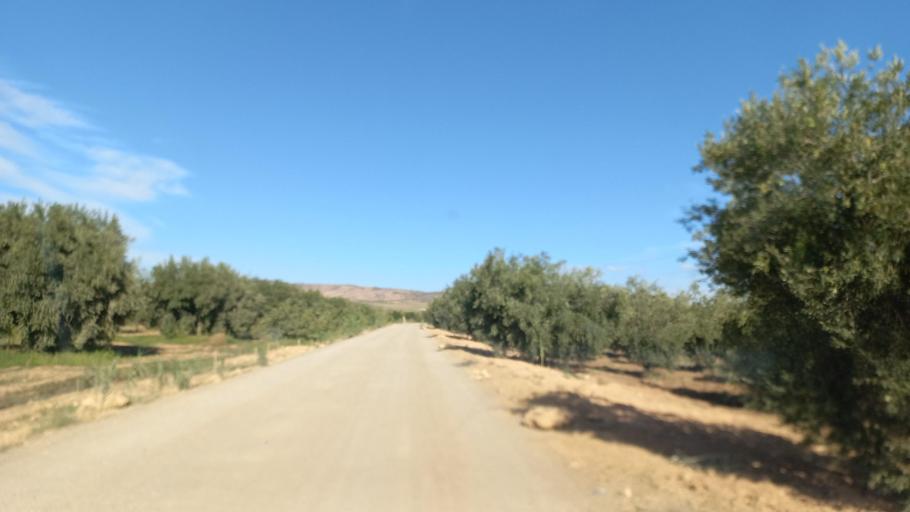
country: TN
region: Al Qasrayn
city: Sbiba
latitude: 35.3014
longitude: 9.0900
